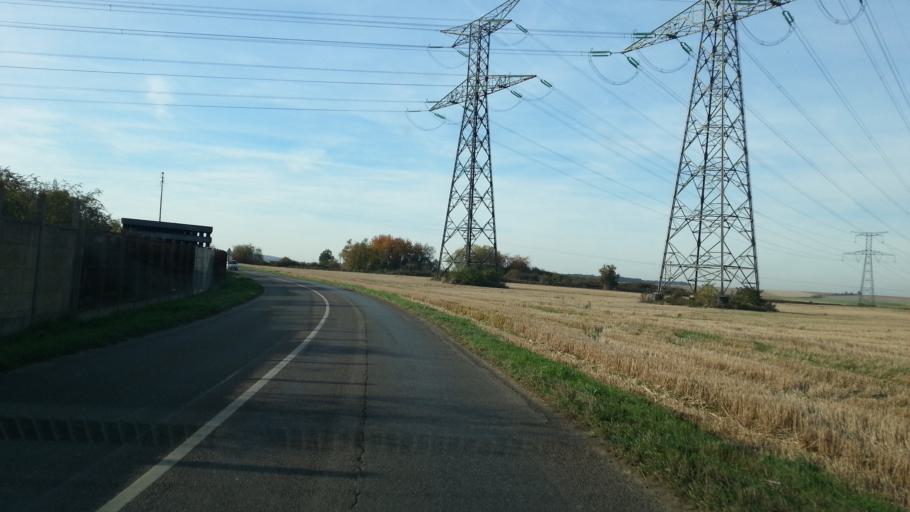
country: FR
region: Ile-de-France
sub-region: Departement du Val-d'Oise
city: Persan
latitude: 49.1661
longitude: 2.2767
